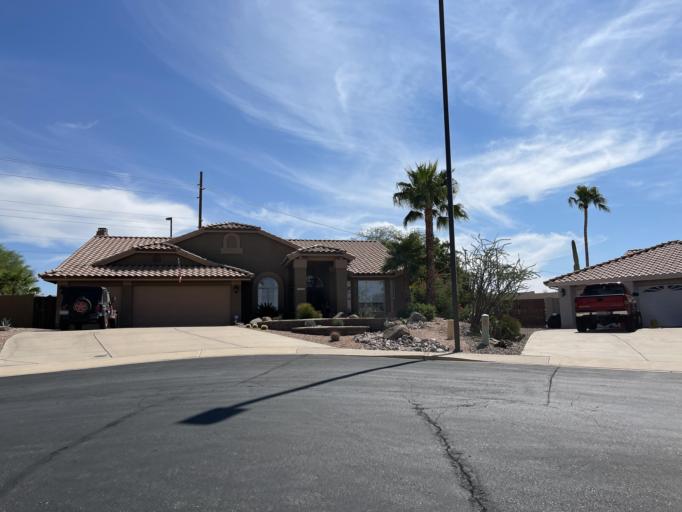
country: US
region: Arizona
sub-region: Maricopa County
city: Fountain Hills
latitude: 33.4908
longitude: -111.6848
